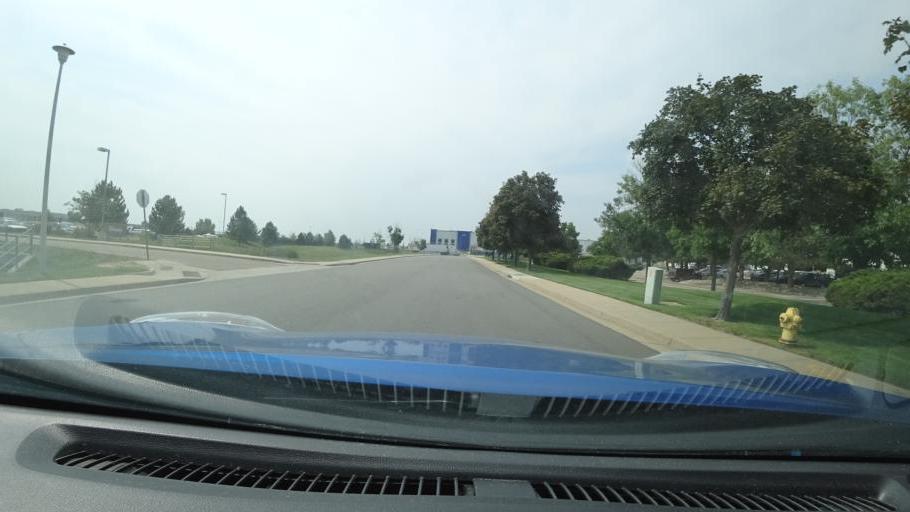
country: US
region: Colorado
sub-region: Adams County
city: Aurora
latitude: 39.7643
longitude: -104.7415
